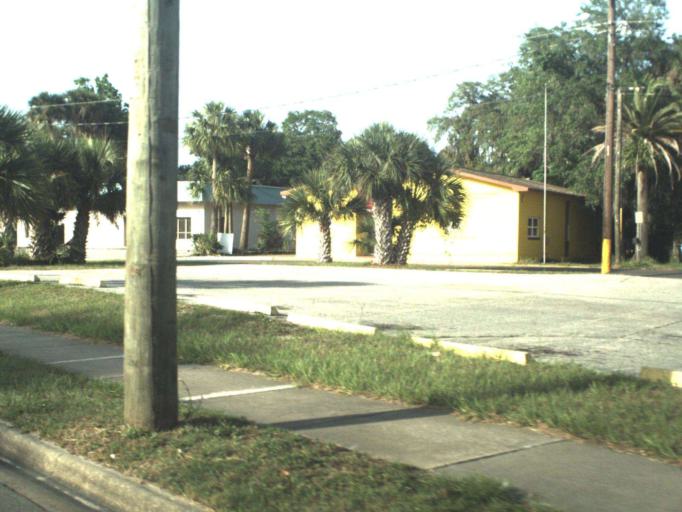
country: US
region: Florida
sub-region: Volusia County
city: New Smyrna Beach
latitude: 29.0287
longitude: -80.9282
